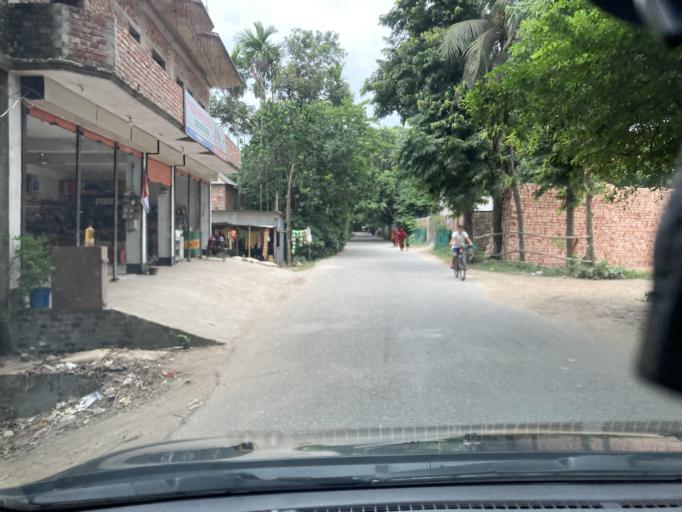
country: BD
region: Dhaka
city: Dohar
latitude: 23.8139
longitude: 90.0469
